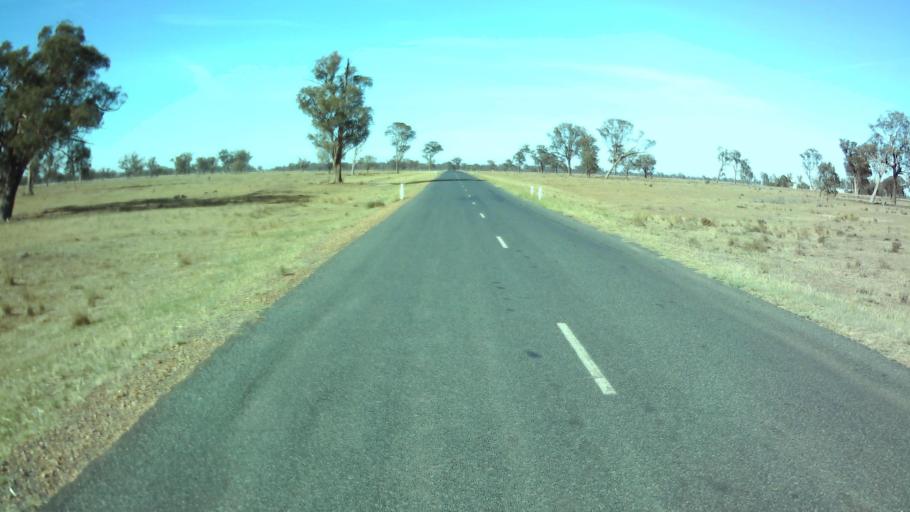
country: AU
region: New South Wales
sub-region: Weddin
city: Grenfell
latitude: -34.0450
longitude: 147.9255
